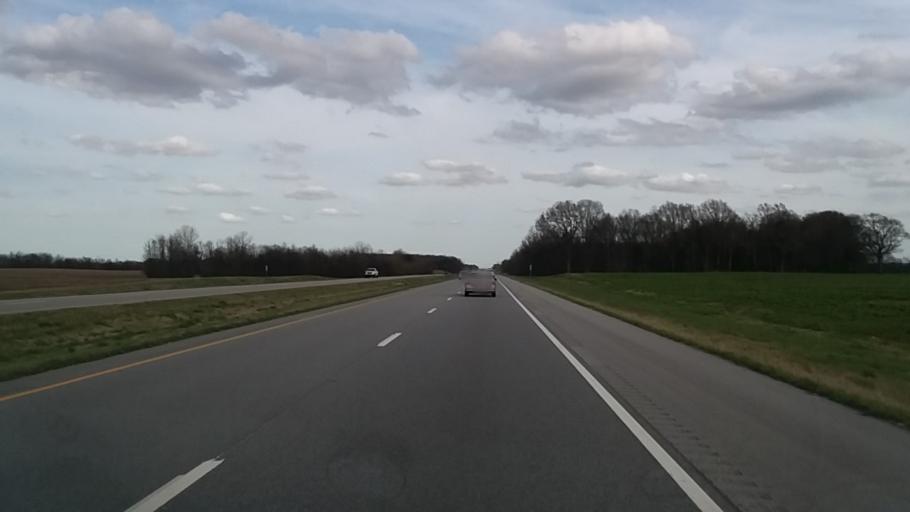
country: US
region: Alabama
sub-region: Lawrence County
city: Town Creek
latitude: 34.6832
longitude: -87.4965
